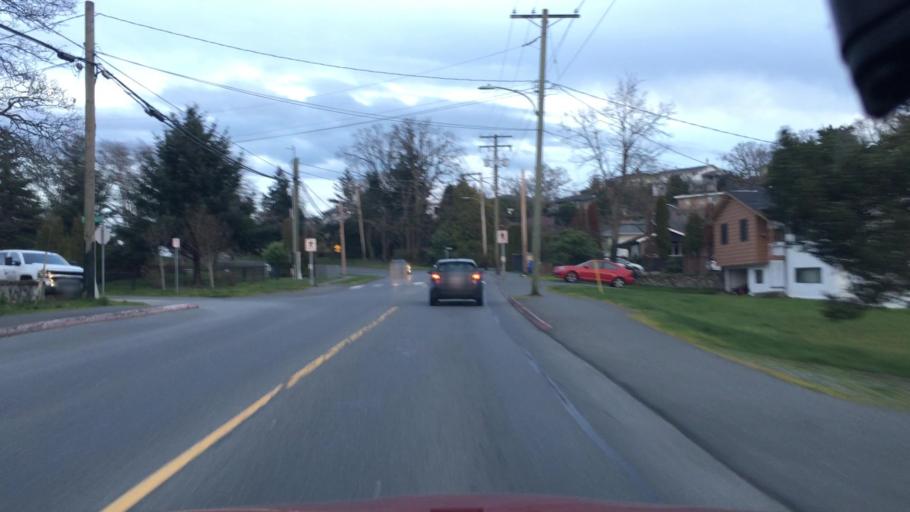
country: CA
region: British Columbia
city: Victoria
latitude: 48.4642
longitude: -123.3426
